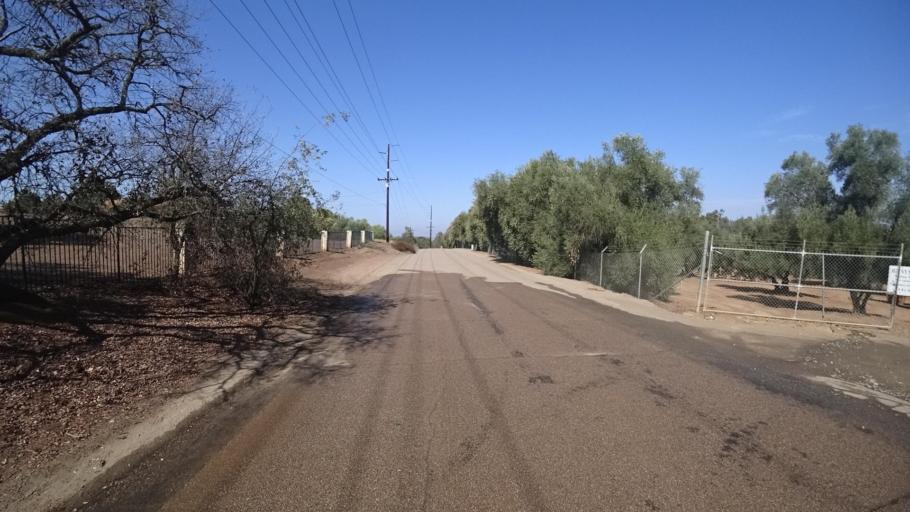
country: US
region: California
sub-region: San Diego County
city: Valley Center
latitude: 33.2857
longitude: -117.0218
